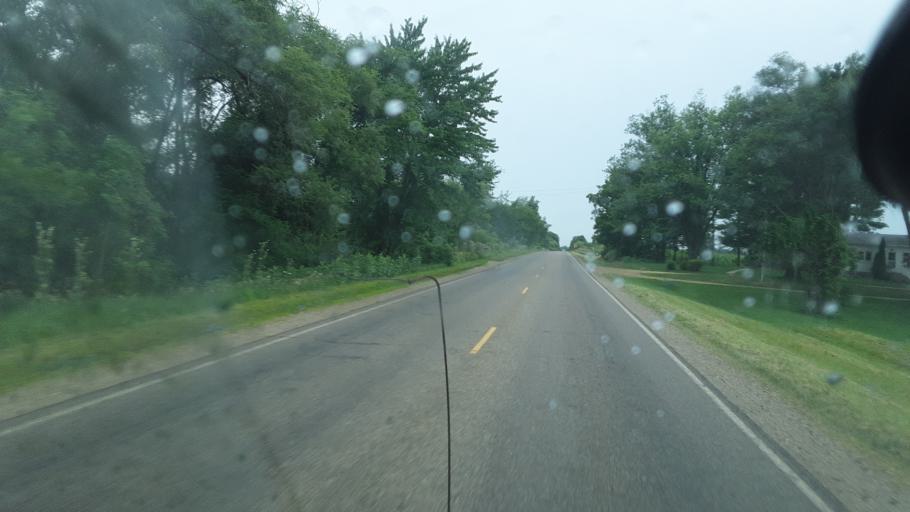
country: US
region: Michigan
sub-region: Hillsdale County
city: Reading
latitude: 41.7076
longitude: -84.7910
